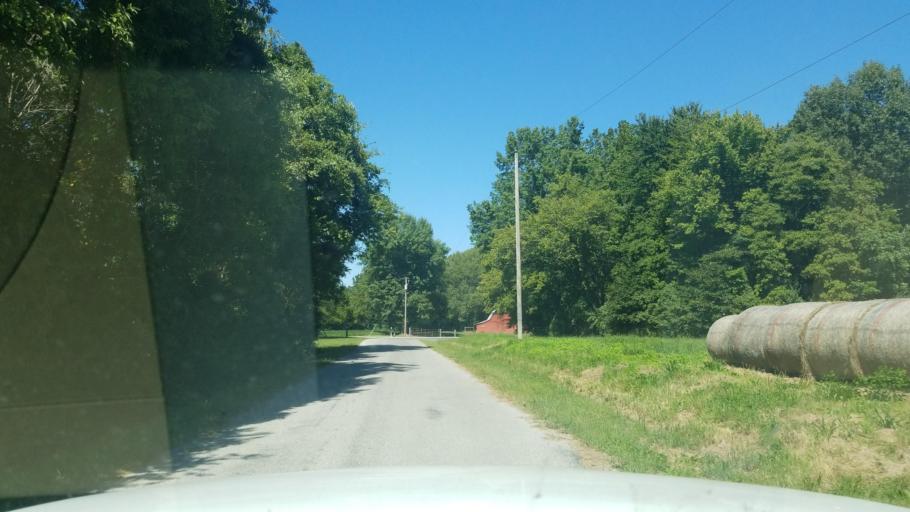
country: US
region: Illinois
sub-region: Saline County
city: Eldorado
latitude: 37.8515
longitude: -88.5165
